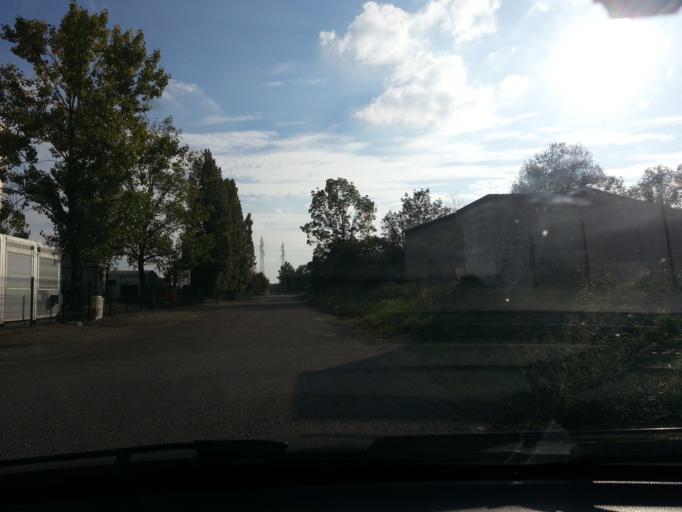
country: FR
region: Bourgogne
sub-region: Departement de Saone-et-Loire
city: Chatenoy-le-Royal
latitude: 46.7999
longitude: 4.7897
